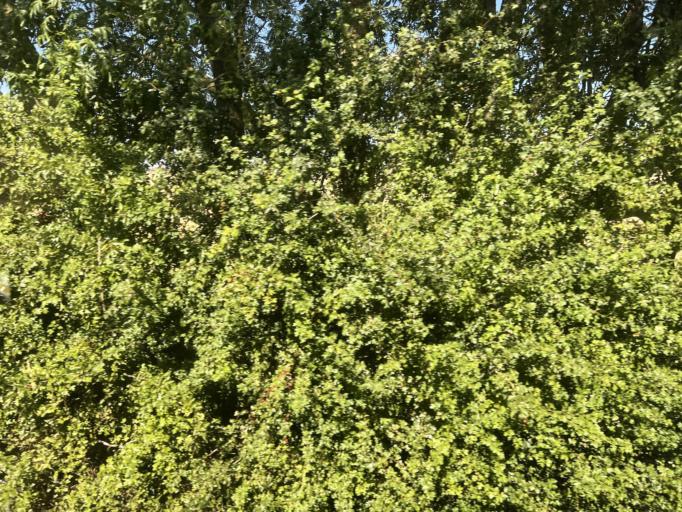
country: GB
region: England
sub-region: Lincolnshire
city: Spilsby
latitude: 53.0674
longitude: 0.0681
